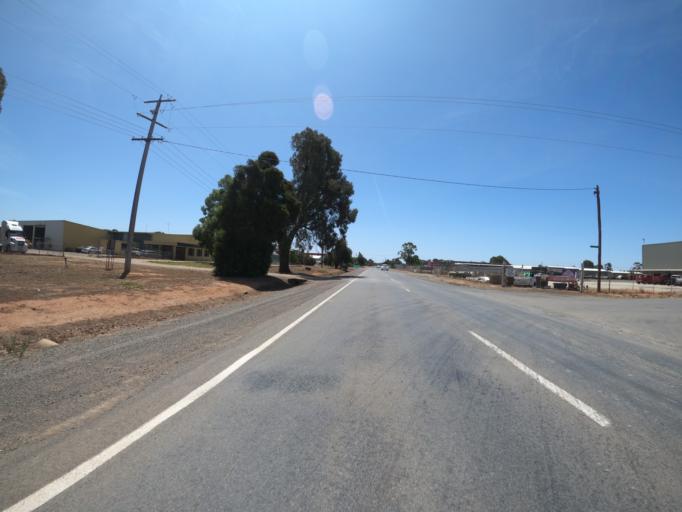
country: AU
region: Victoria
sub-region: Moira
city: Yarrawonga
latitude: -36.0307
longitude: 145.9955
